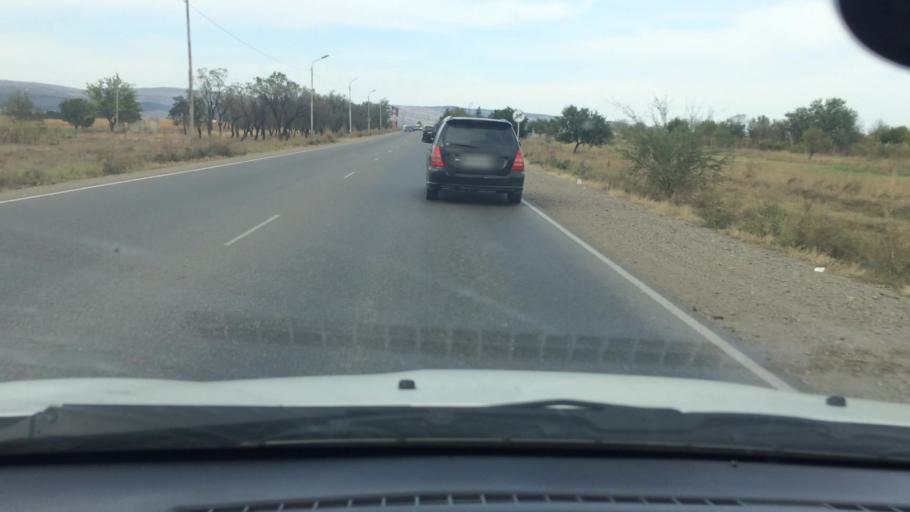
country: GE
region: Kvemo Kartli
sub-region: Marneuli
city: Marneuli
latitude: 41.5879
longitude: 44.7794
